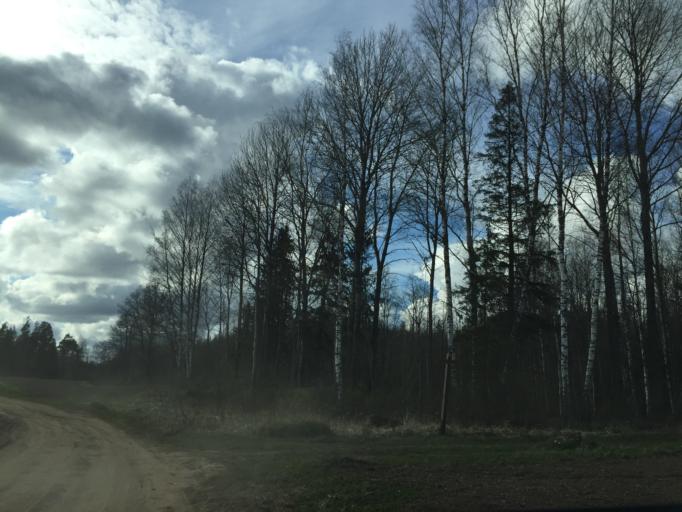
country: LV
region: Burtnieki
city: Matisi
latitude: 57.6189
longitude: 24.9934
